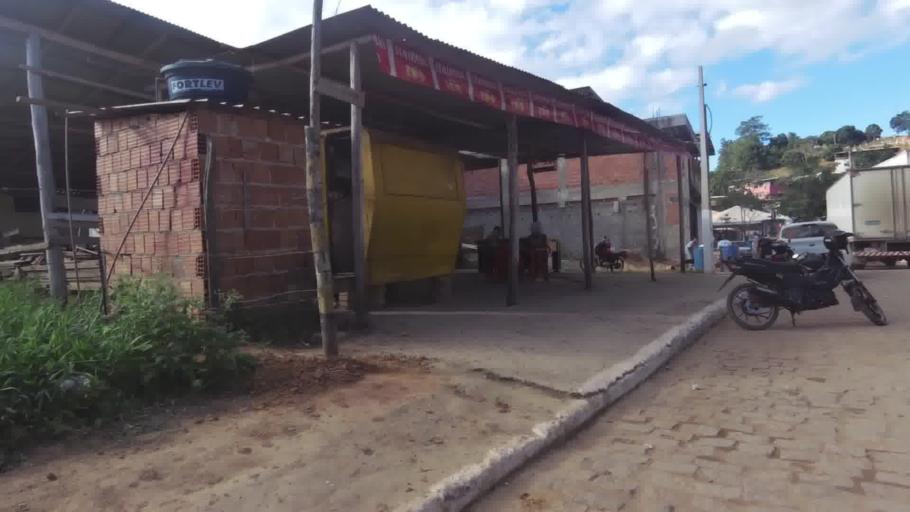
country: BR
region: Espirito Santo
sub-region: Marataizes
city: Marataizes
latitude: -21.1006
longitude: -41.0455
